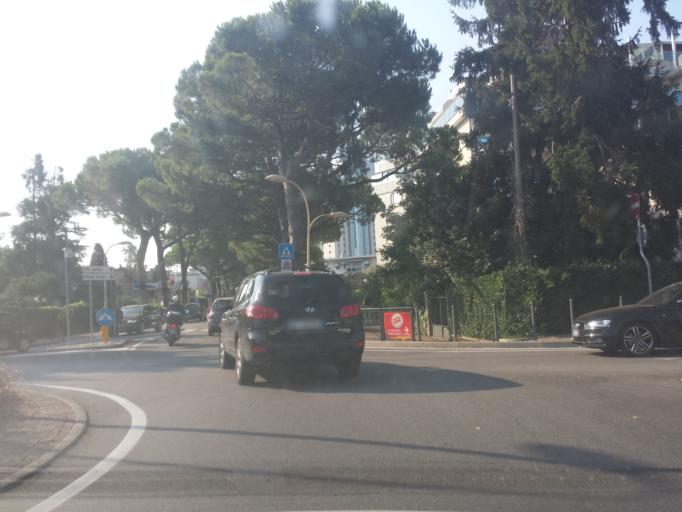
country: IT
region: Veneto
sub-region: Provincia di Venezia
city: Lido di Iesolo
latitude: 45.5104
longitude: 12.6434
